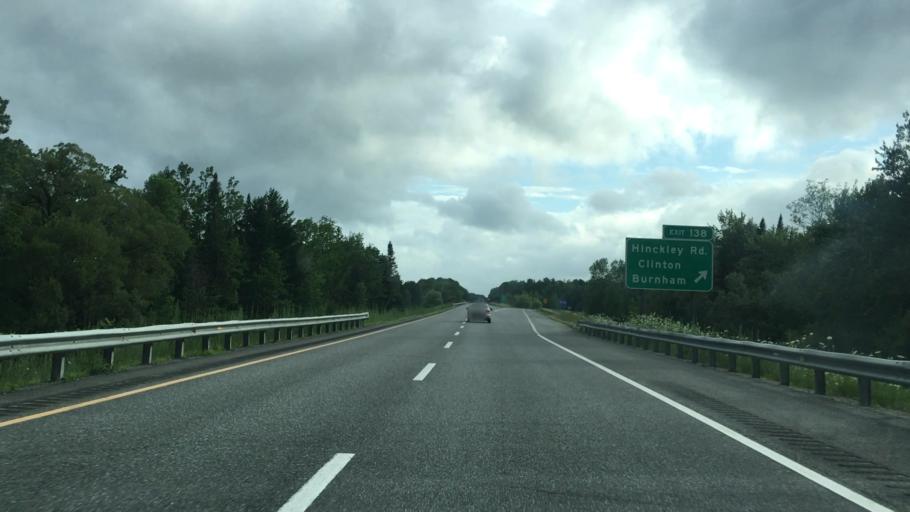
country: US
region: Maine
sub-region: Kennebec County
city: Clinton
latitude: 44.6435
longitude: -69.5248
